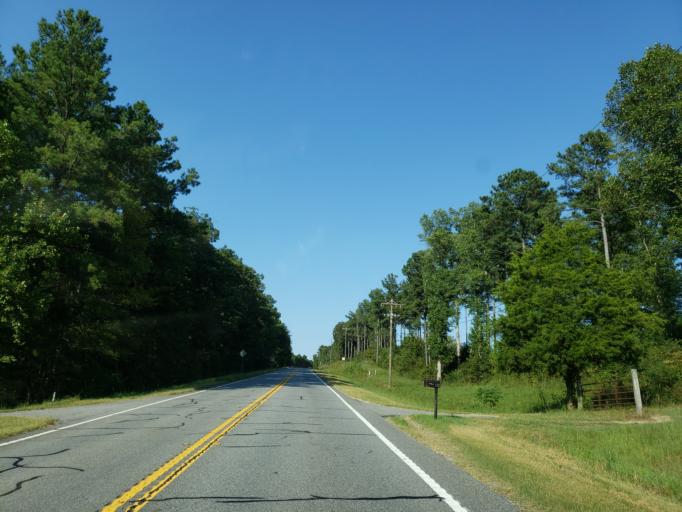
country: US
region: Georgia
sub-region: Whitfield County
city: Varnell
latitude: 34.8970
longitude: -84.9053
